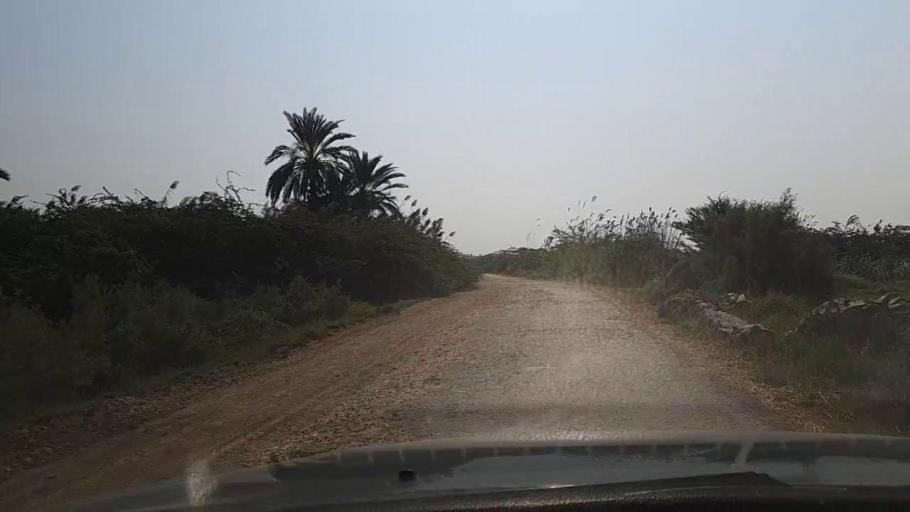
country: PK
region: Sindh
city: Mirpur Sakro
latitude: 24.3918
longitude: 67.6650
